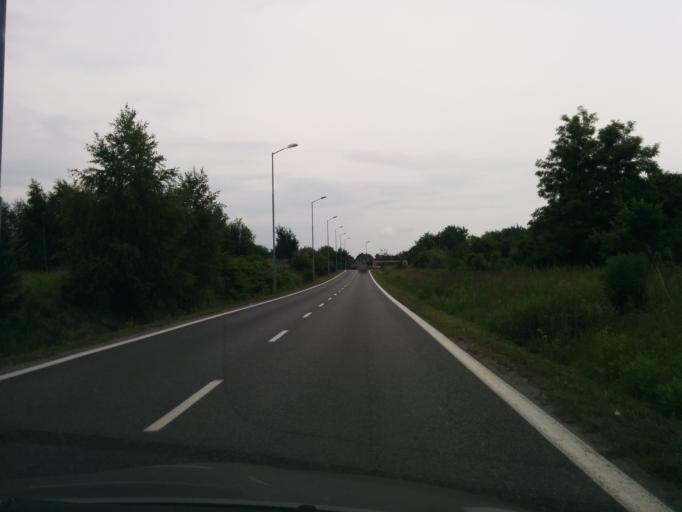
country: PL
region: Silesian Voivodeship
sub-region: Ruda Slaska
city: Ruda Slaska
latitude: 50.2569
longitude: 18.8406
